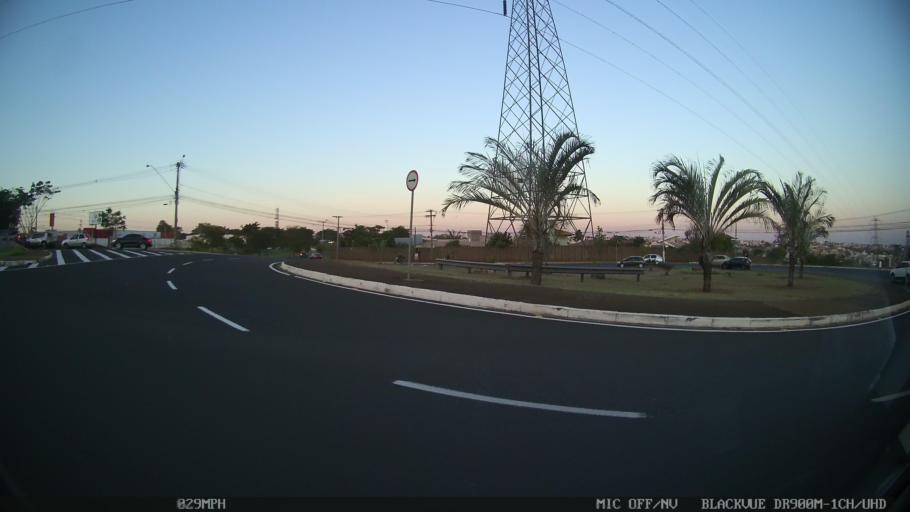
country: BR
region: Sao Paulo
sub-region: Sao Jose Do Rio Preto
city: Sao Jose do Rio Preto
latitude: -20.8023
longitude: -49.3453
